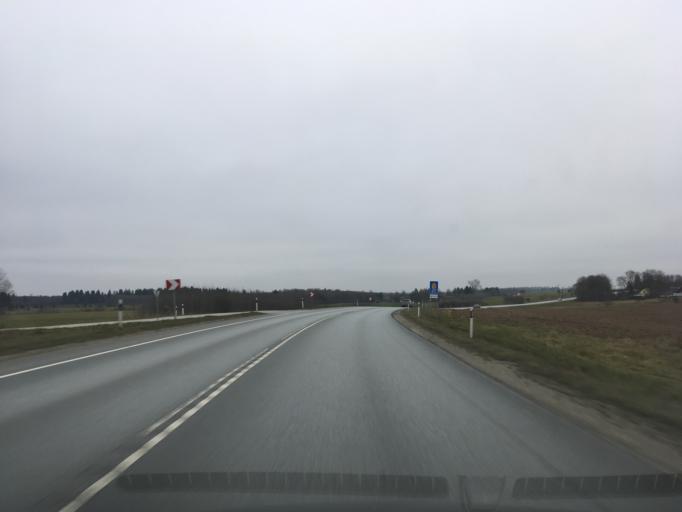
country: EE
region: Laeaene-Virumaa
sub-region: Viru-Nigula vald
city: Kunda
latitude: 59.4199
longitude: 26.6576
